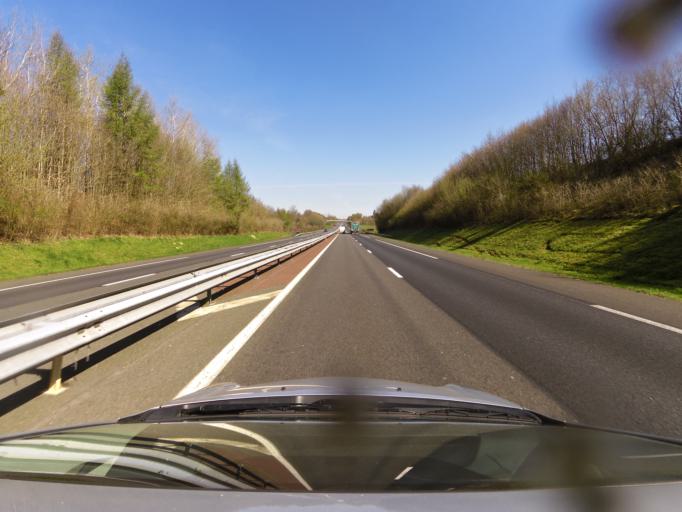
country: FR
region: Lower Normandy
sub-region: Departement de la Manche
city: Villedieu-les-Poeles
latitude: 48.8016
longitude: -1.2619
